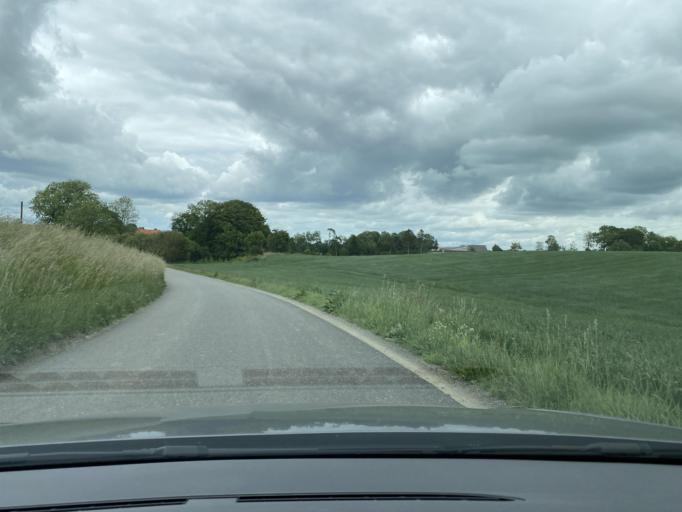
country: DK
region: South Denmark
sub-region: Vejle Kommune
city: Vejle
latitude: 55.6604
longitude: 9.4793
